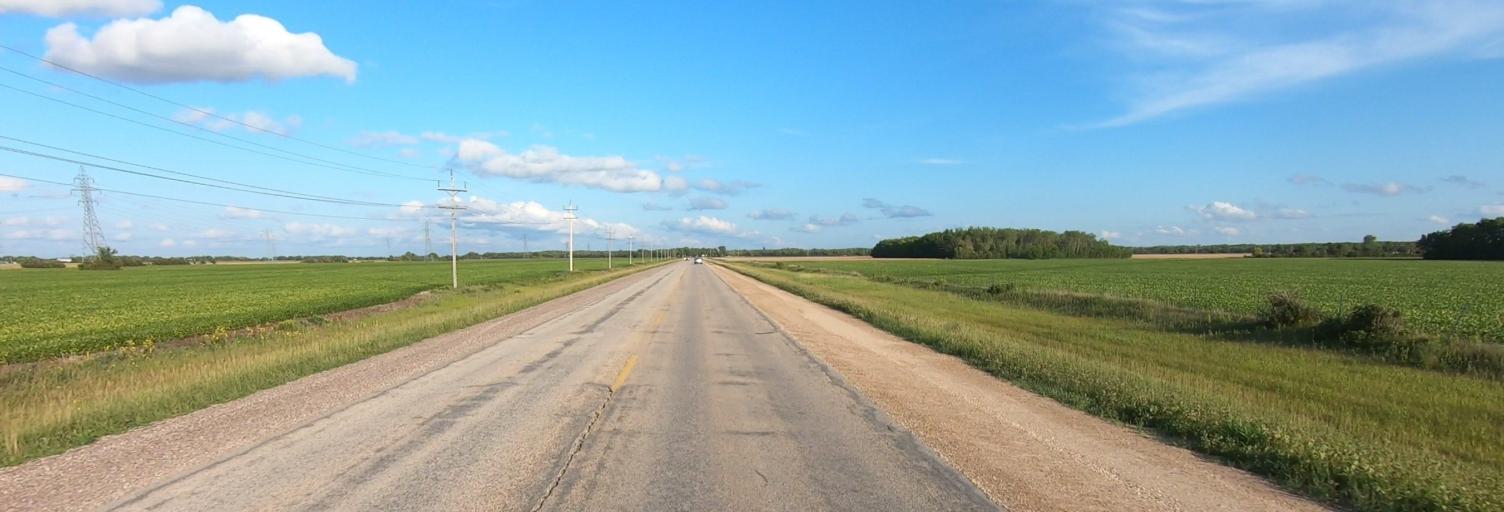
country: CA
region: Manitoba
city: Selkirk
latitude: 50.1197
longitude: -96.8538
